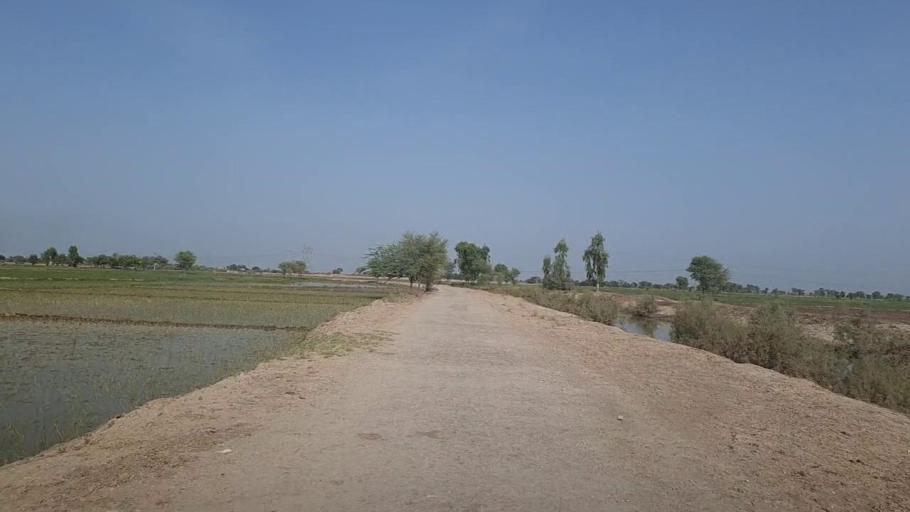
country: PK
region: Sindh
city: Sita Road
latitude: 27.0903
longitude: 67.8506
